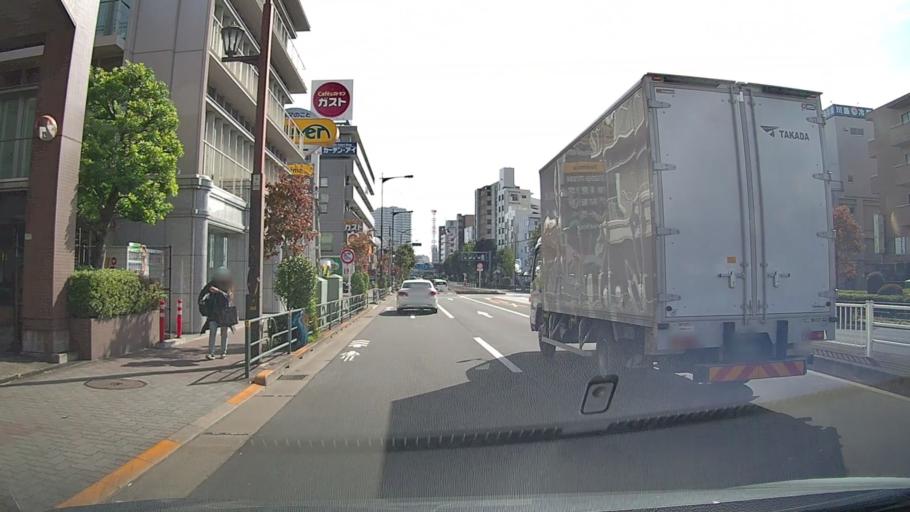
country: JP
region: Saitama
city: Wako
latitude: 35.7399
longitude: 139.6389
